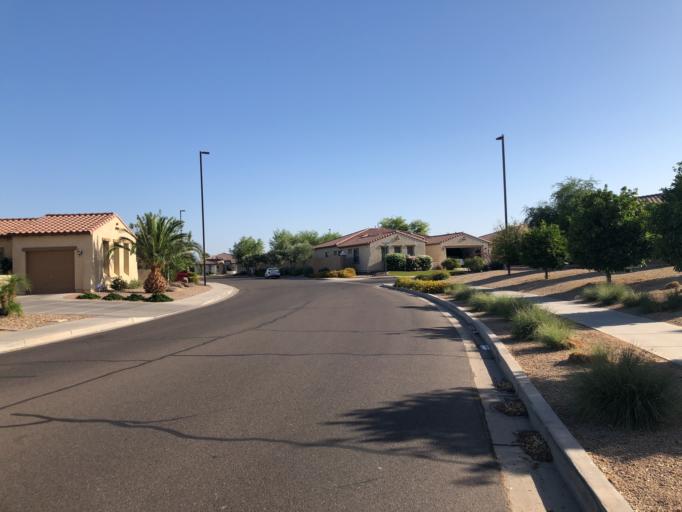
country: US
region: Arizona
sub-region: Maricopa County
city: Queen Creek
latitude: 33.2297
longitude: -111.7172
